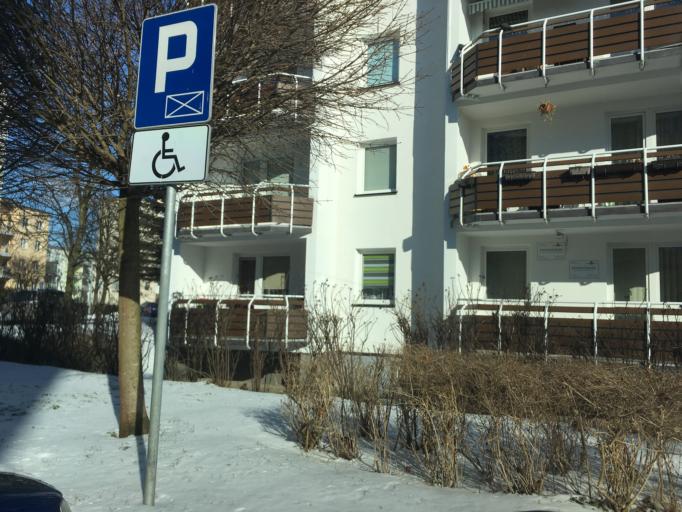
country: PL
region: Pomeranian Voivodeship
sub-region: Powiat slupski
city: Kobylnica
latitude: 54.4601
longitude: 16.9955
